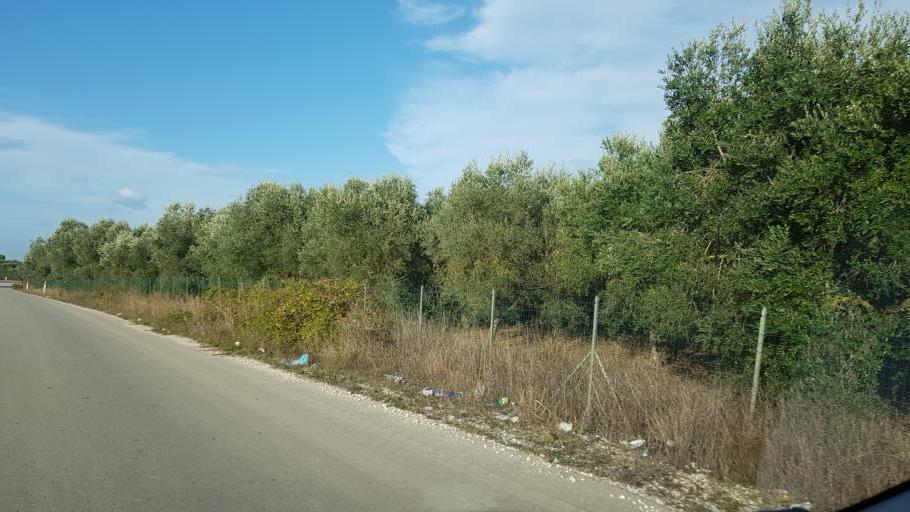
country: IT
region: Apulia
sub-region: Provincia di Brindisi
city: Oria
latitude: 40.5318
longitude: 17.6558
